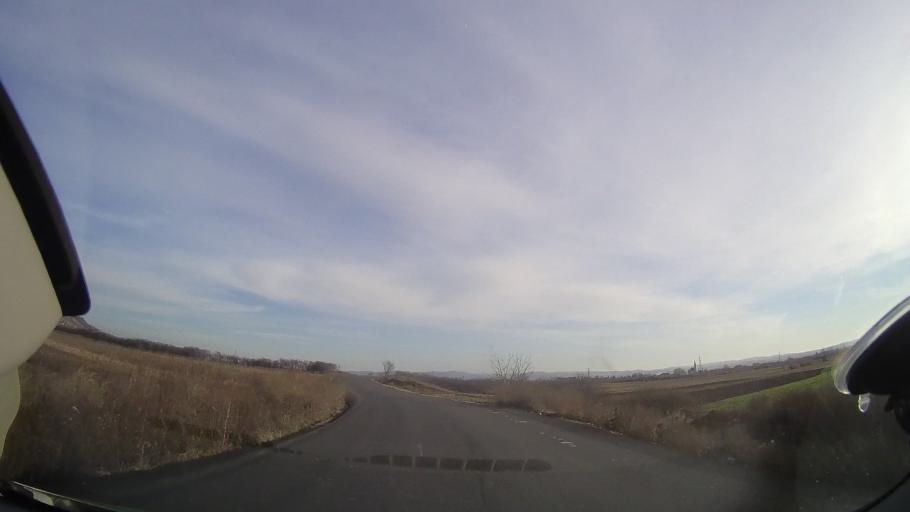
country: RO
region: Bihor
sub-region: Comuna Tileagd
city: Tileagd
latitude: 47.0854
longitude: 22.1833
